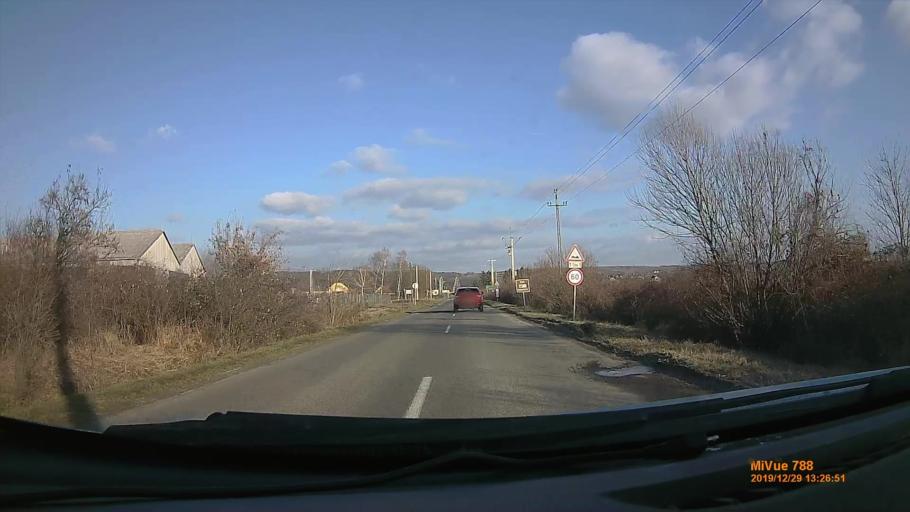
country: HU
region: Heves
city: Verpelet
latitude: 47.8521
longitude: 20.2099
